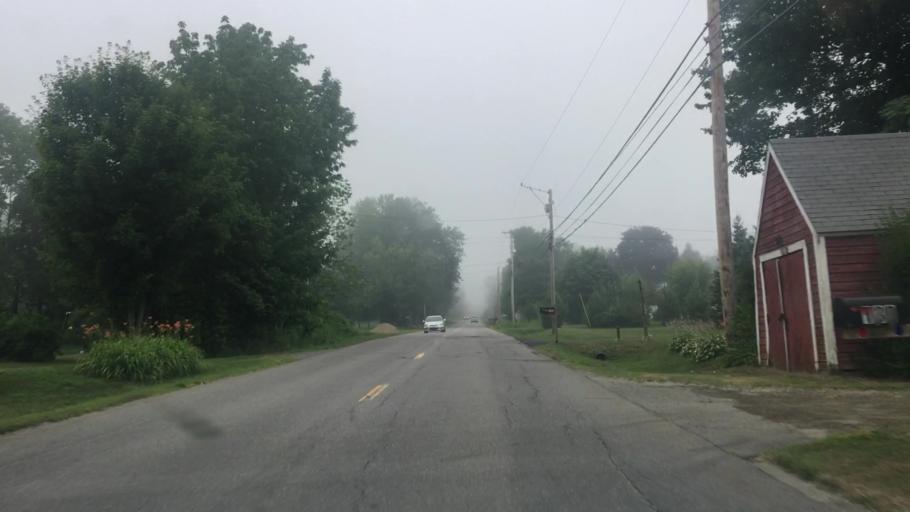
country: US
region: Maine
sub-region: Kennebec County
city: Oakland
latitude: 44.5231
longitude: -69.7263
